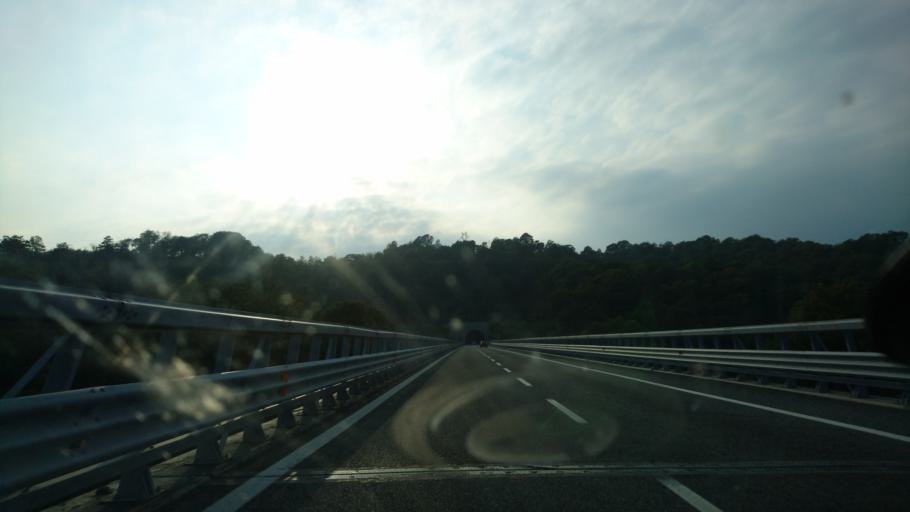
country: IT
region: Liguria
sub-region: Provincia di Savona
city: Altare
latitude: 44.3427
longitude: 8.3536
